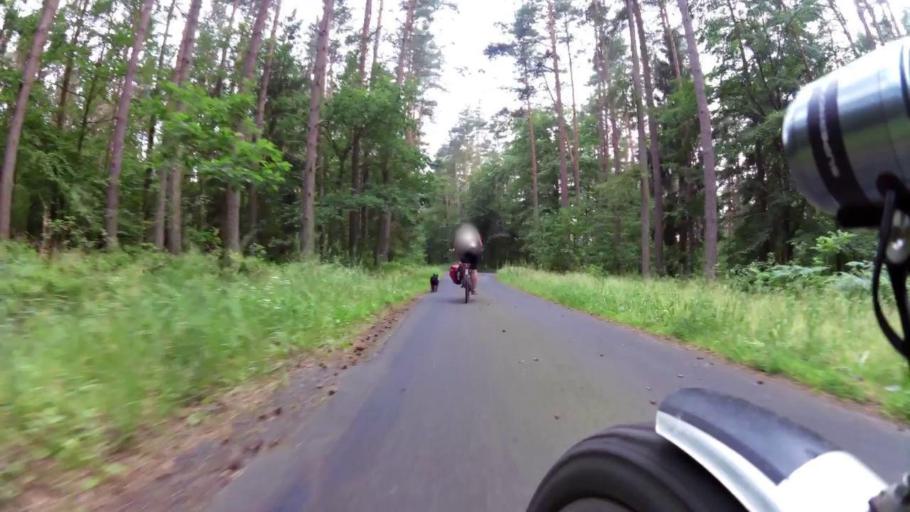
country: PL
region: West Pomeranian Voivodeship
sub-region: Powiat policki
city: Police
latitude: 53.6347
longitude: 14.4734
